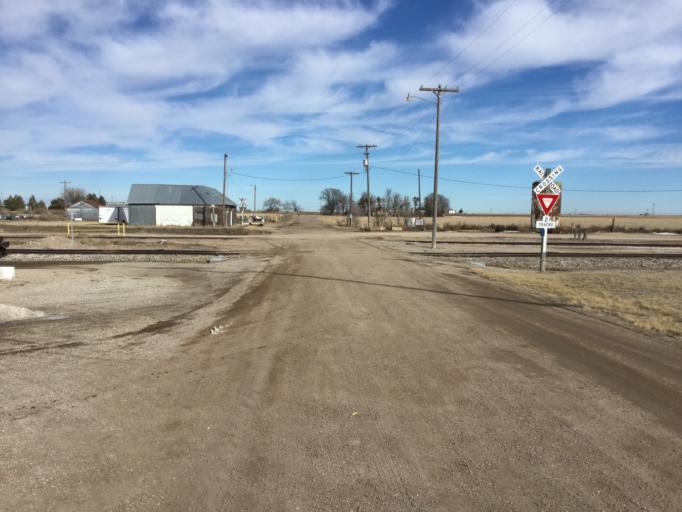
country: US
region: Kansas
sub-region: Lane County
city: Dighton
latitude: 38.4860
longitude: -100.4617
